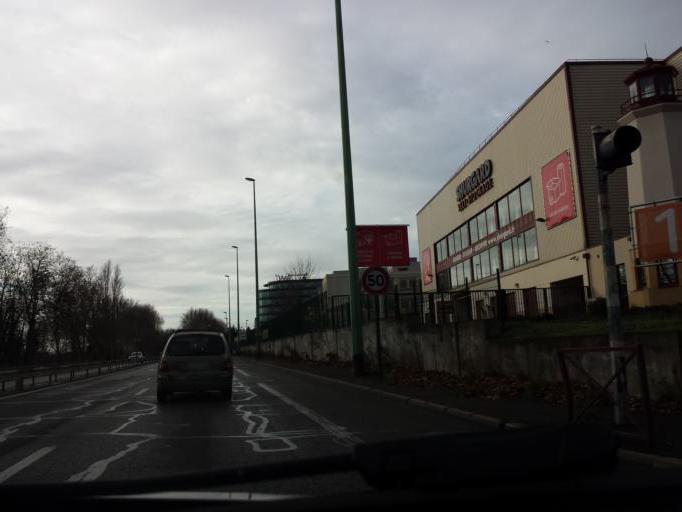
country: FR
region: Ile-de-France
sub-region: Departement du Val-d'Oise
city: Bezons
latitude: 48.9261
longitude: 2.2264
